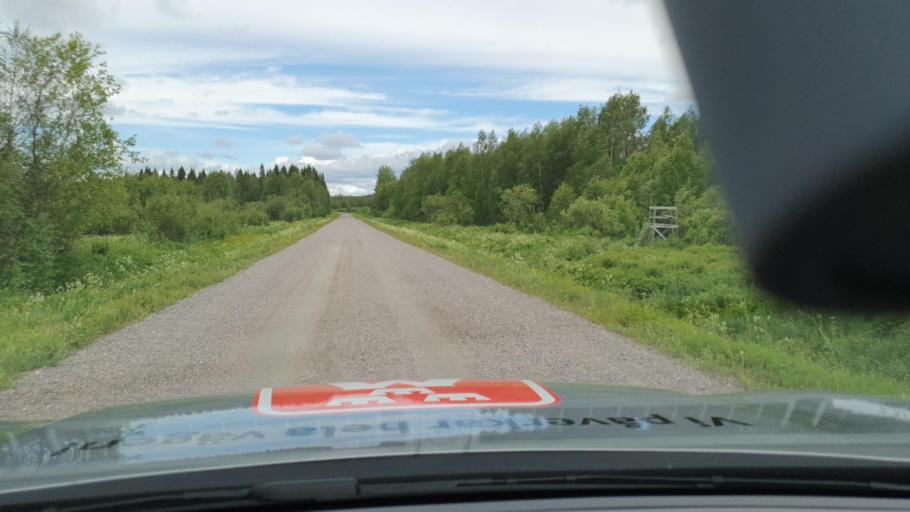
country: FI
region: Lapland
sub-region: Torniolaakso
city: Ylitornio
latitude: 65.9759
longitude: 23.7948
